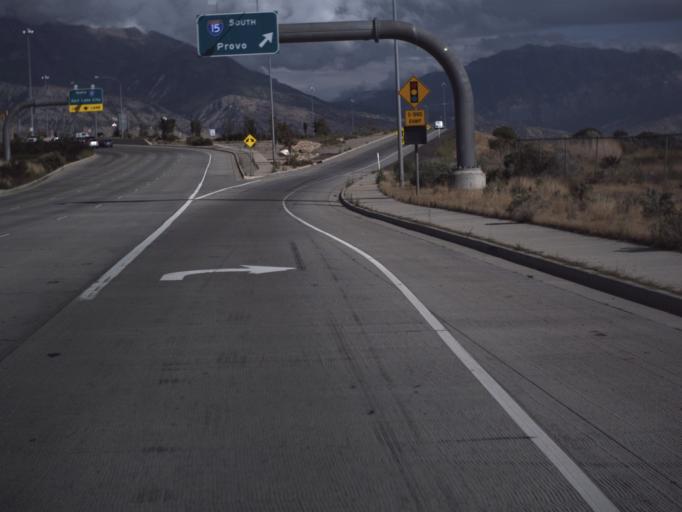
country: US
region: Utah
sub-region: Utah County
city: American Fork
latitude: 40.3767
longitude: -111.8235
